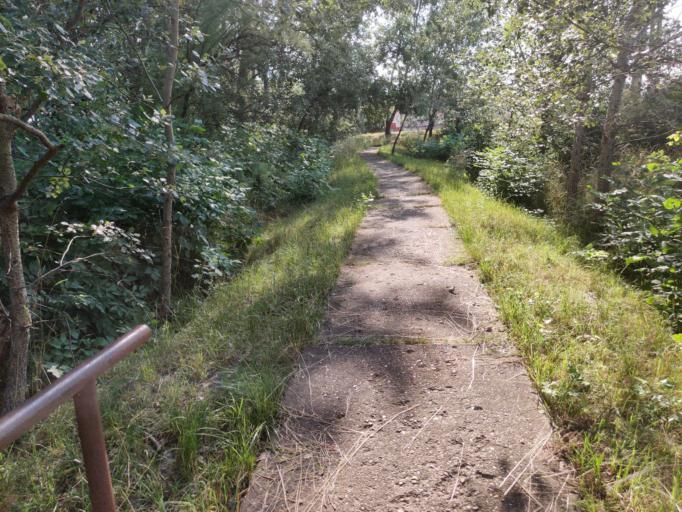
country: HU
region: Hajdu-Bihar
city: Balmazujvaros
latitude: 47.6169
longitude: 21.3321
